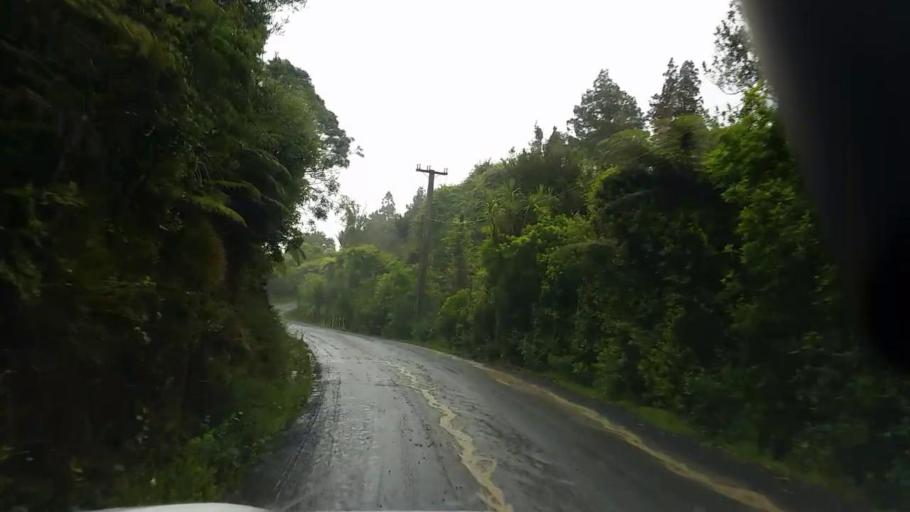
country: NZ
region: Auckland
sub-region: Auckland
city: Muriwai Beach
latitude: -36.8568
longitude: 174.4845
